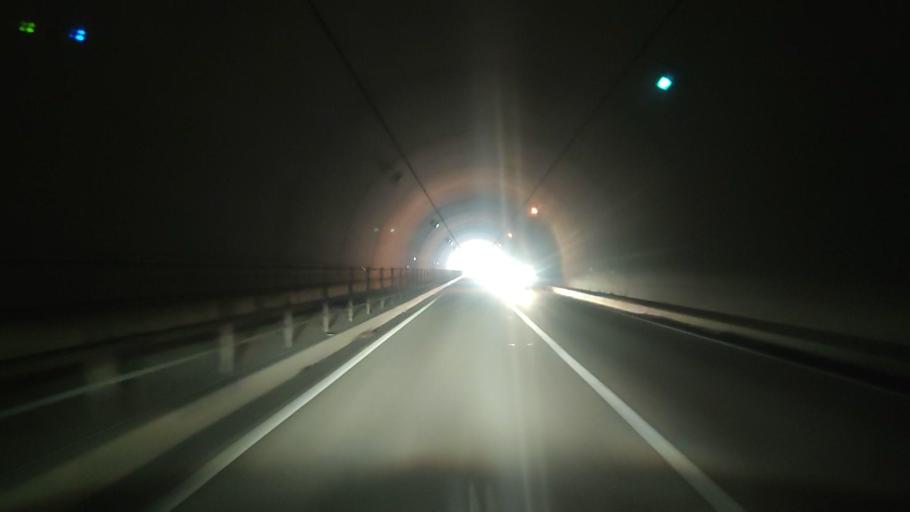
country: JP
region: Oita
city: Saiki
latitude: 32.7954
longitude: 131.9129
